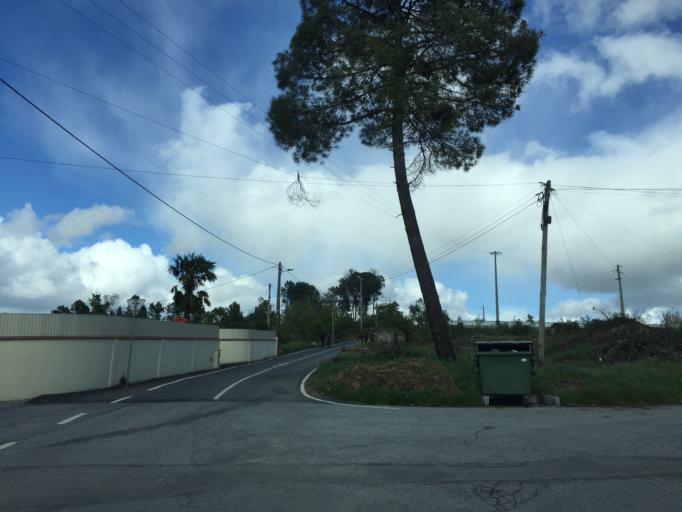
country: PT
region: Viseu
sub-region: Viseu
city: Abraveses
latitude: 40.6611
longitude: -7.9437
